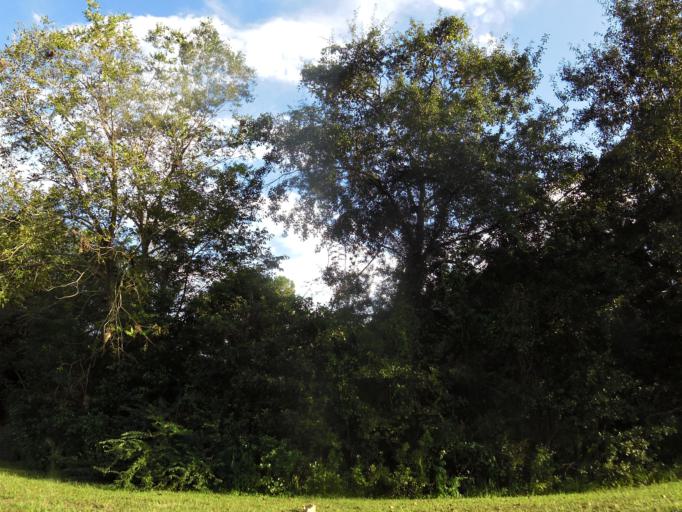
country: US
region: Georgia
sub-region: Lowndes County
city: Remerton
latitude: 30.8198
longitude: -83.3034
